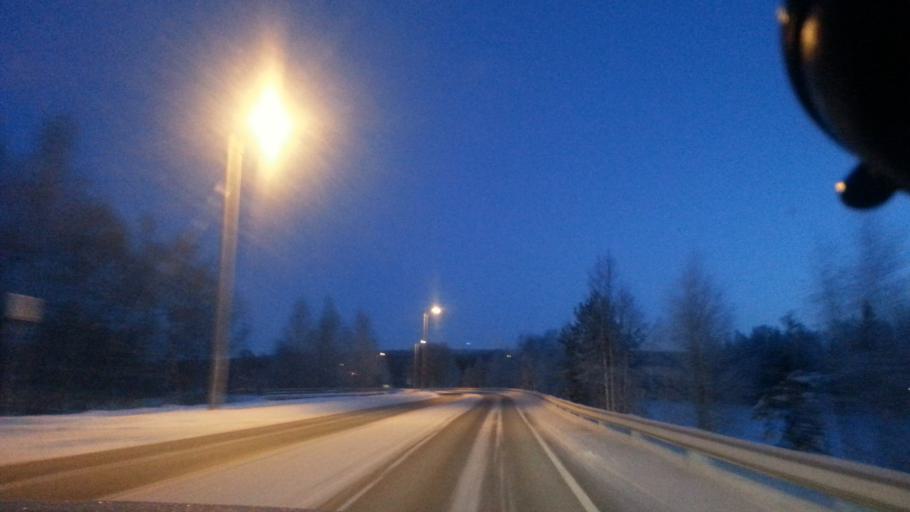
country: FI
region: Lapland
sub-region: Rovaniemi
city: Rovaniemi
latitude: 66.4837
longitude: 25.7477
